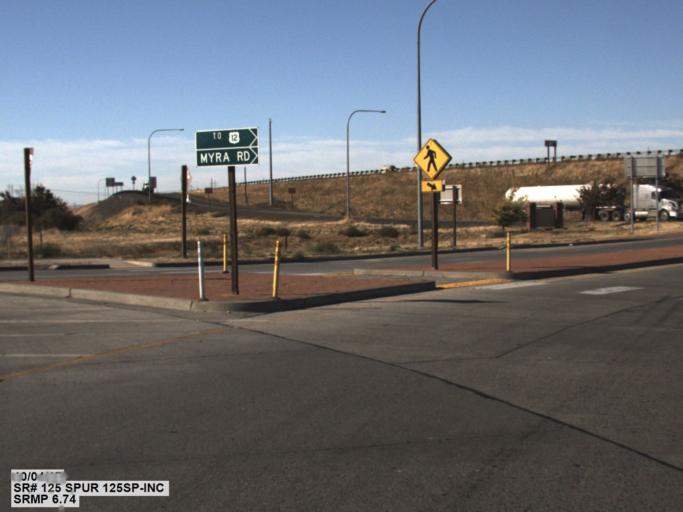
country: US
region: Washington
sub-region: Walla Walla County
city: College Place
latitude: 46.0097
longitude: -118.3900
